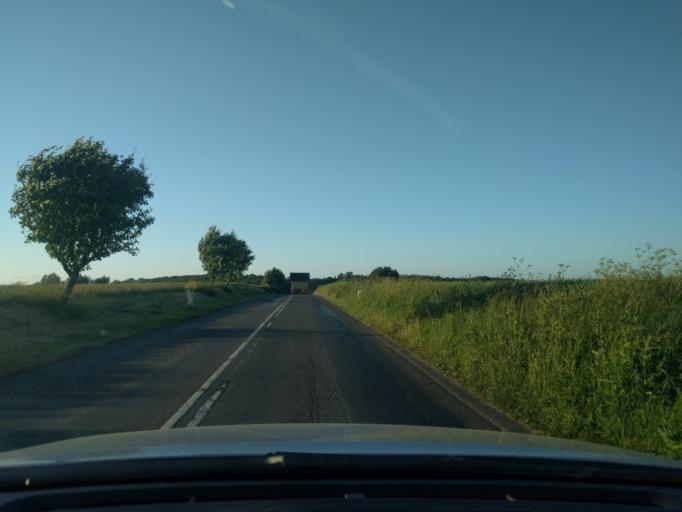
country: DK
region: South Denmark
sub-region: Kerteminde Kommune
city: Kerteminde
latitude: 55.5674
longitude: 10.6464
